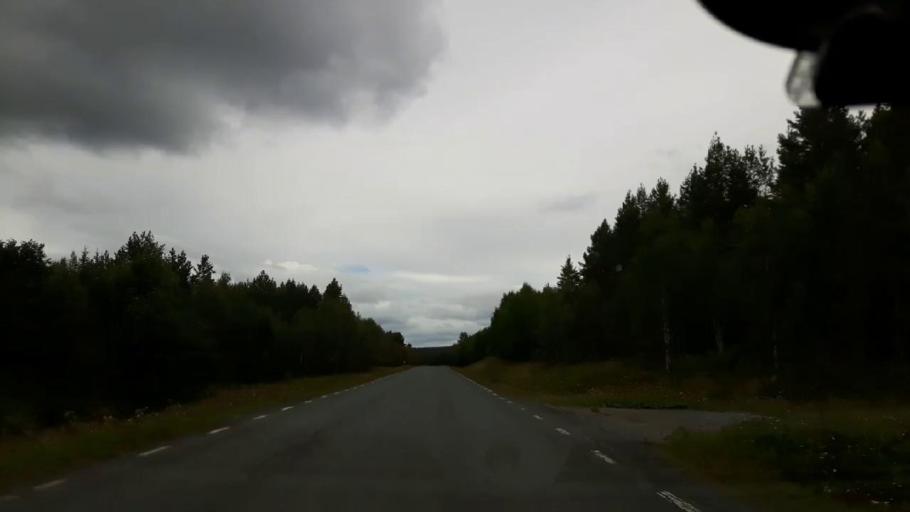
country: SE
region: Jaemtland
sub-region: Krokoms Kommun
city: Valla
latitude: 63.6299
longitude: 13.8166
